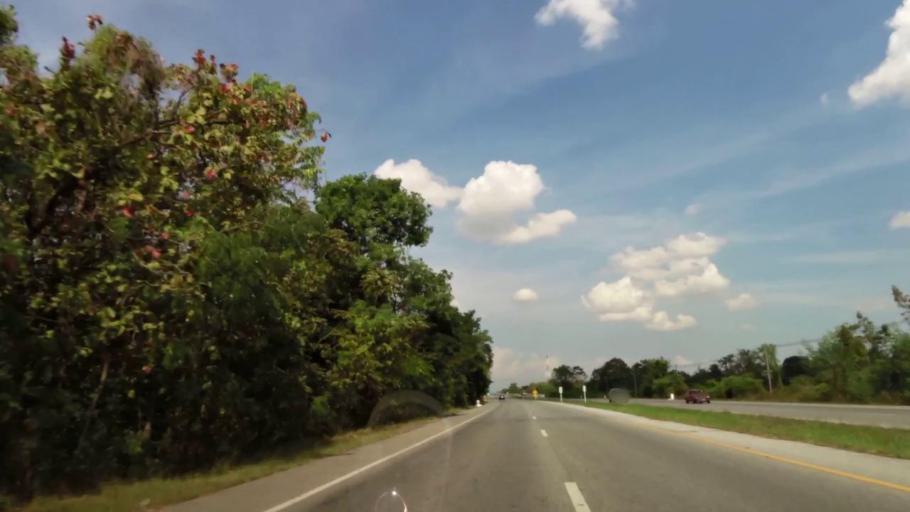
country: TH
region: Uttaradit
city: Thong Saen Khan
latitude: 17.4601
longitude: 100.2377
